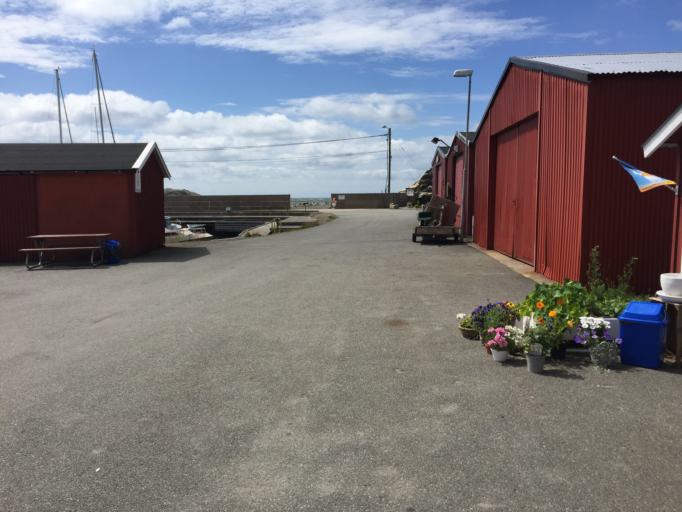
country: SE
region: Vaestra Goetaland
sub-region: Goteborg
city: Styrso
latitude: 57.6178
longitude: 11.7611
